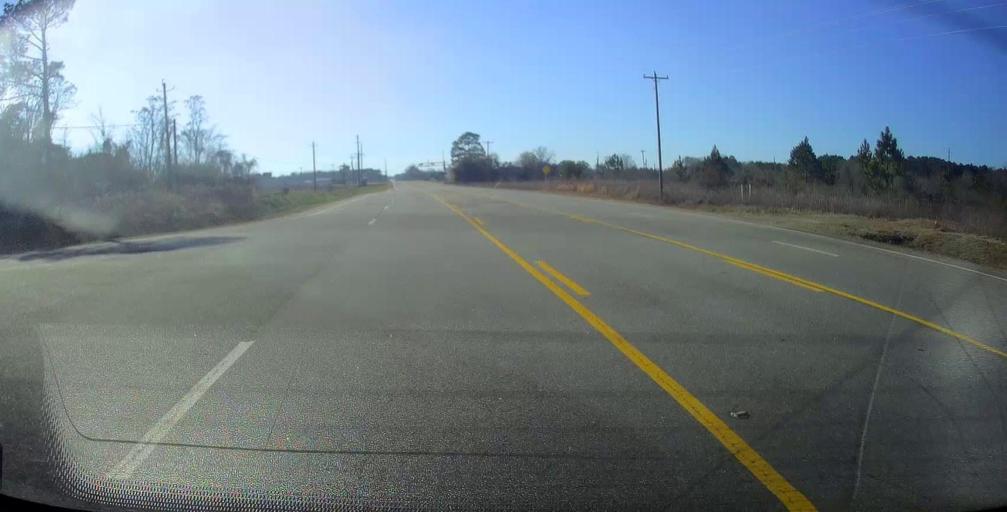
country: US
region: Georgia
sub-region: Sumter County
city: Americus
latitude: 32.1191
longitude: -84.1936
